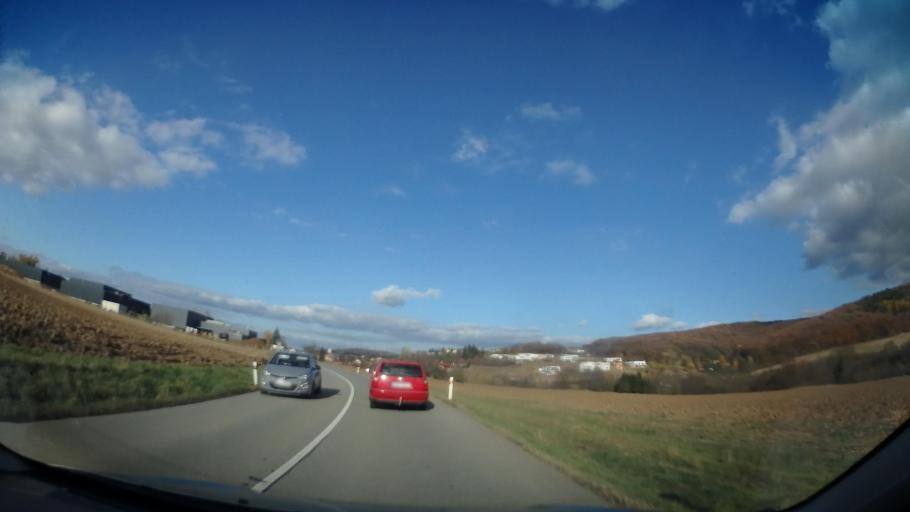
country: CZ
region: South Moravian
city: Kurim
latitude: 49.2590
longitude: 16.5276
